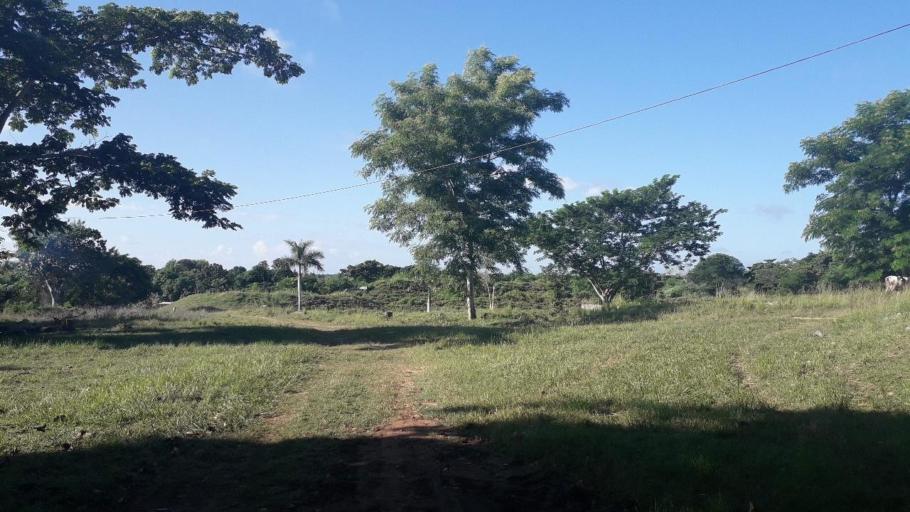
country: CU
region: La Habana
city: Boyeros
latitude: 23.0289
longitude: -82.4114
